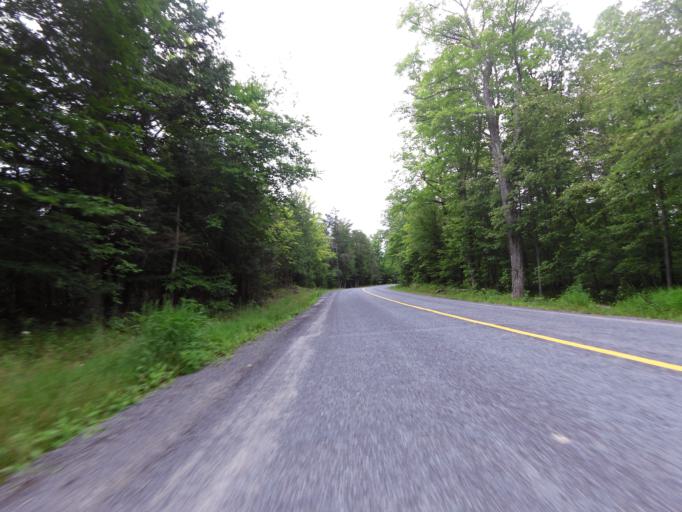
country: CA
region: Ontario
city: Perth
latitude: 44.8763
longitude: -76.5341
